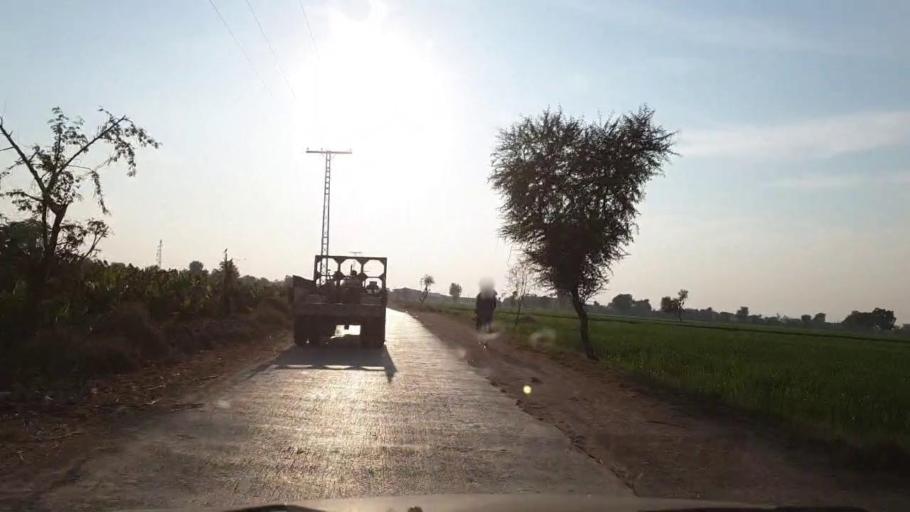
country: PK
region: Sindh
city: Khadro
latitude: 26.1529
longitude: 68.7236
